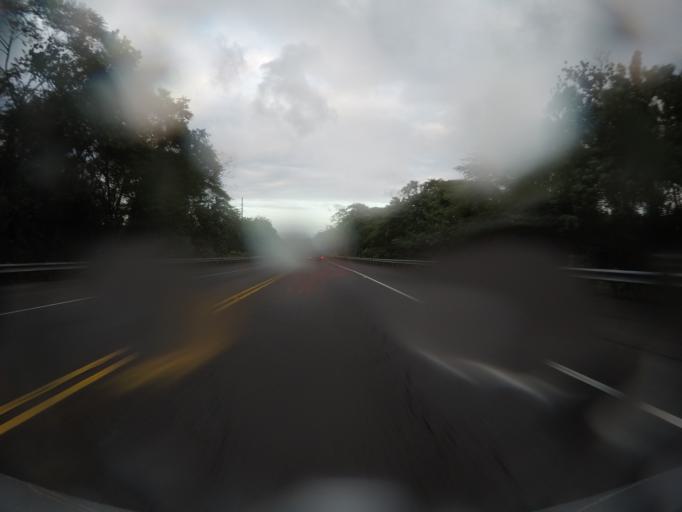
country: US
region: Hawaii
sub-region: Hawaii County
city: Hilo
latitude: 19.6806
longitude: -155.1245
